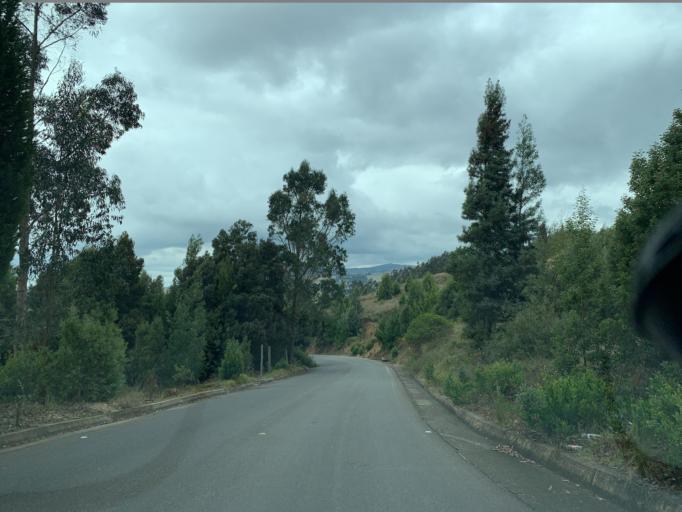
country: CO
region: Boyaca
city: Tunja
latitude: 5.5676
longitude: -73.3621
